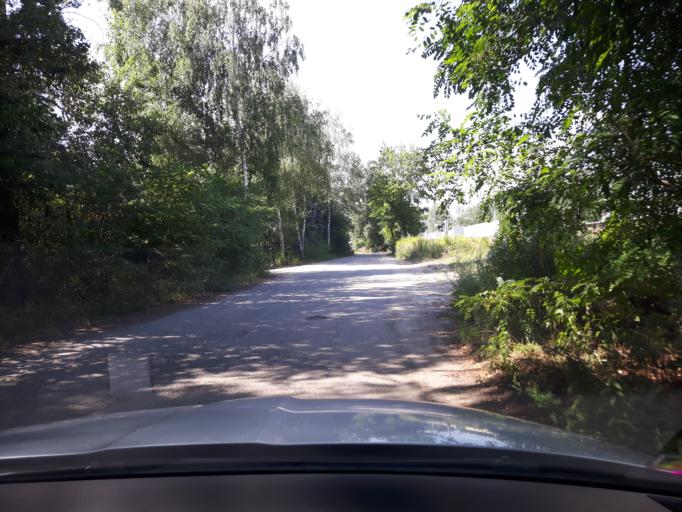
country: PL
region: Masovian Voivodeship
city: Zielonka
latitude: 52.2907
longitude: 21.1546
